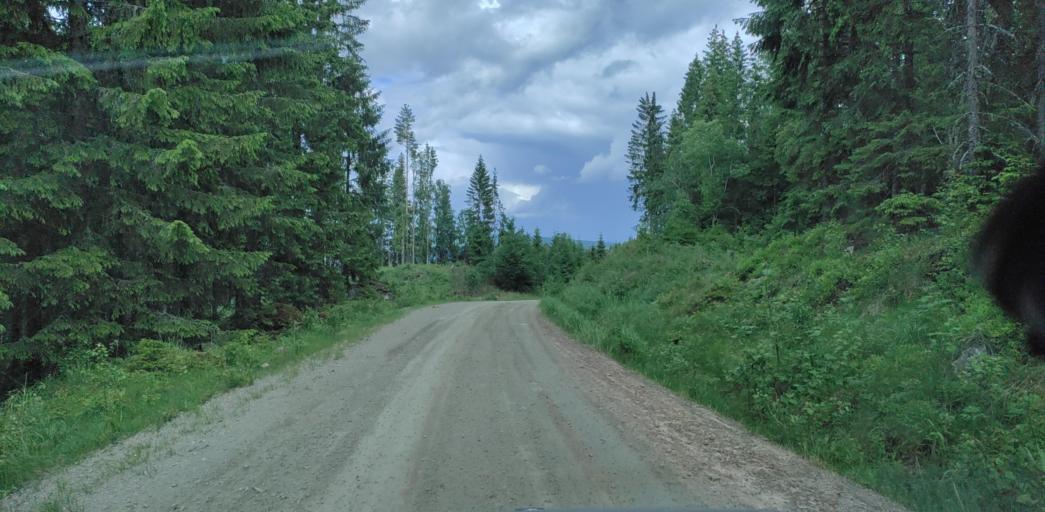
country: SE
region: Vaermland
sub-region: Munkfors Kommun
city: Munkfors
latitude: 59.9624
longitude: 13.4179
